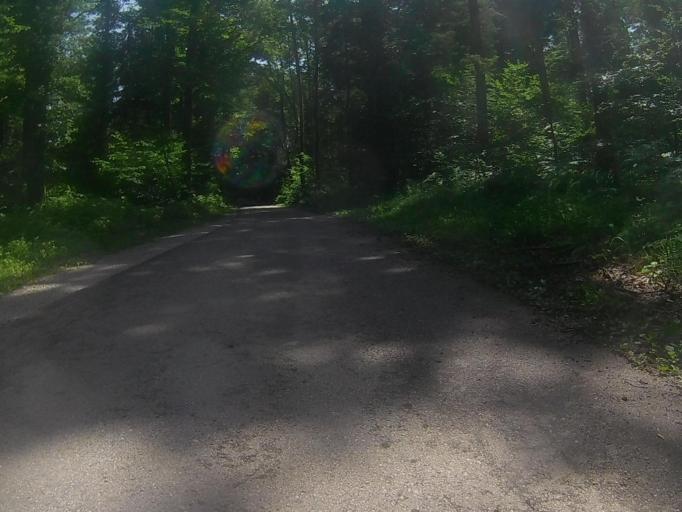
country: SI
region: Hoce-Slivnica
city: Radizel
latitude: 46.4811
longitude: 15.6385
